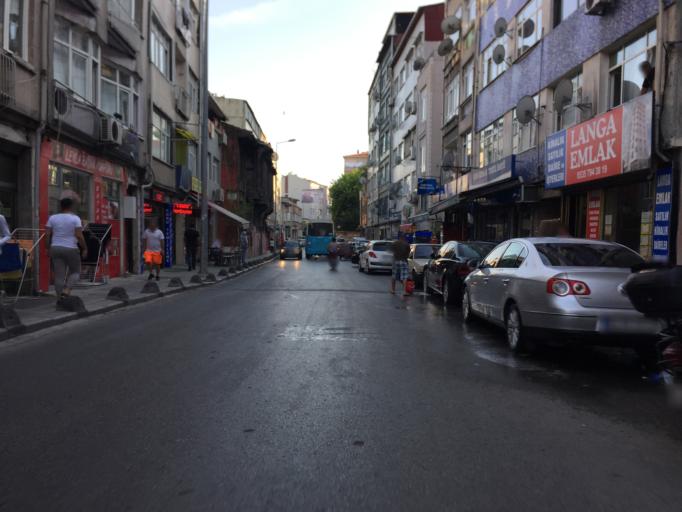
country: TR
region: Istanbul
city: Istanbul
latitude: 41.0059
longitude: 28.9457
